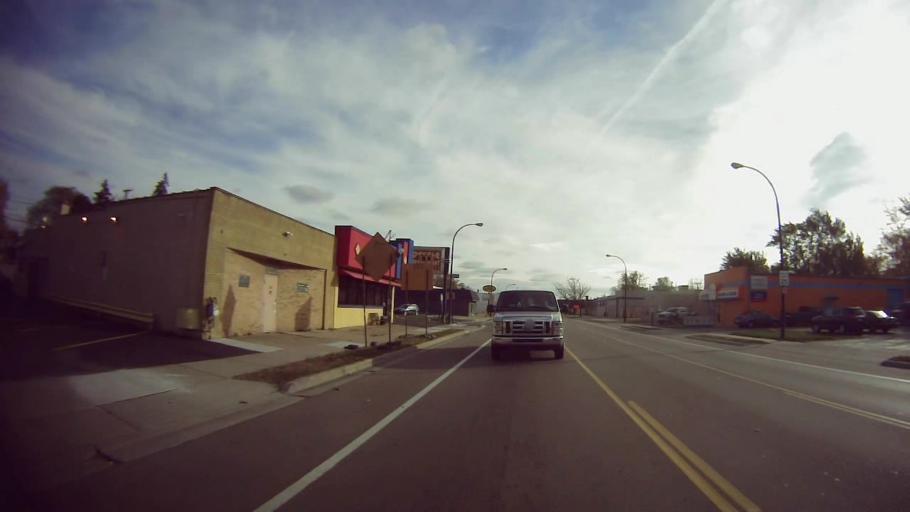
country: US
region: Michigan
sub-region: Oakland County
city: Hazel Park
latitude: 42.4612
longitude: -83.1130
